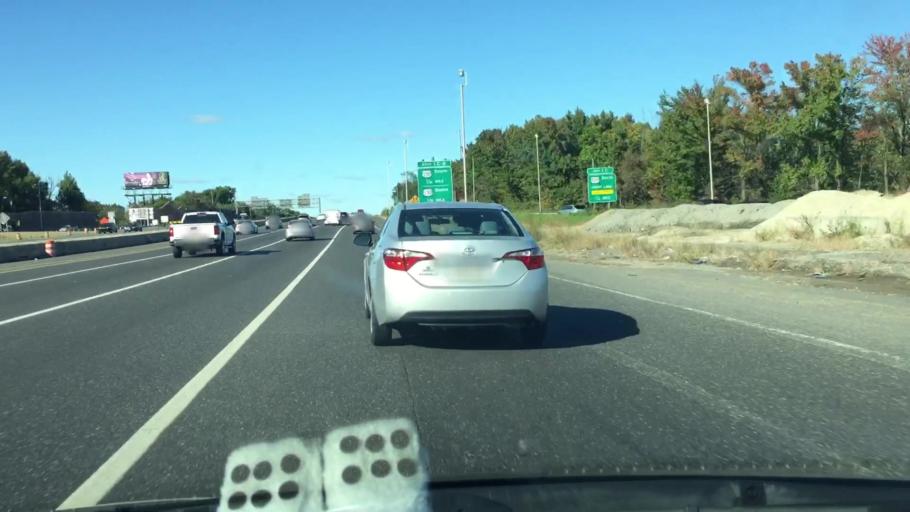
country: US
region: New Jersey
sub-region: Camden County
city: Mount Ephraim
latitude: 39.8755
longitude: -75.1022
